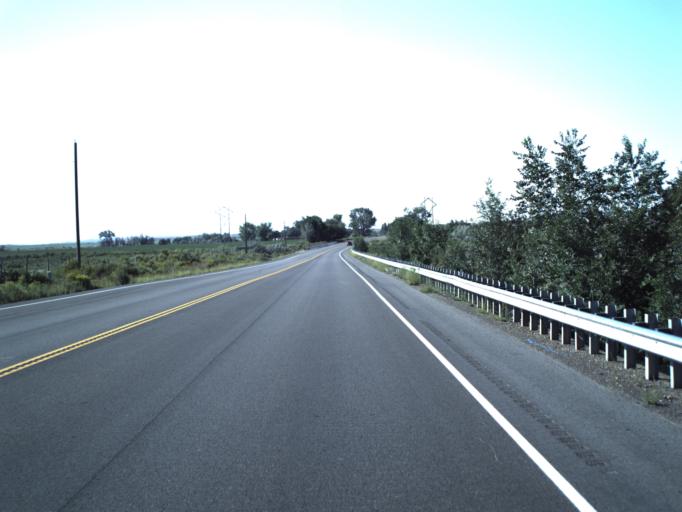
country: US
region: Utah
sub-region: Emery County
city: Huntington
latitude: 39.3040
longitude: -110.9643
